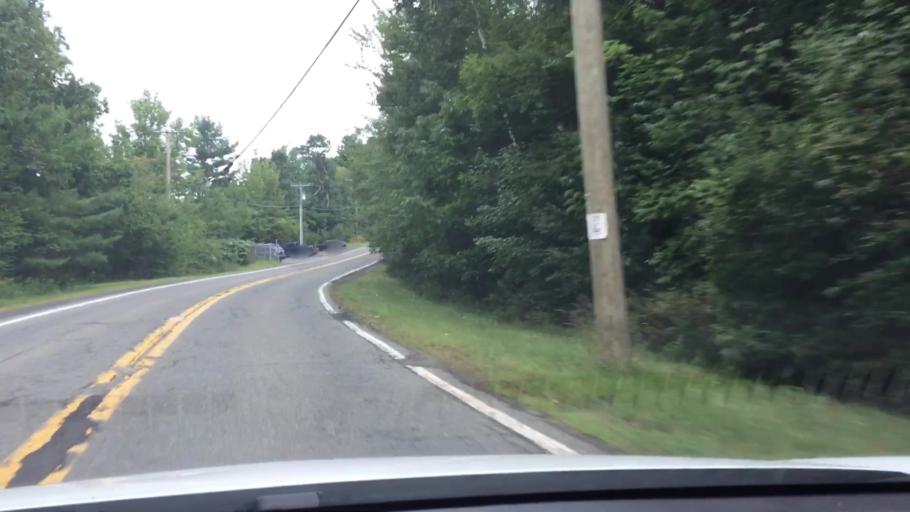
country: US
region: Massachusetts
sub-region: Hampden County
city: Granville
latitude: 42.1955
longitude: -72.9358
